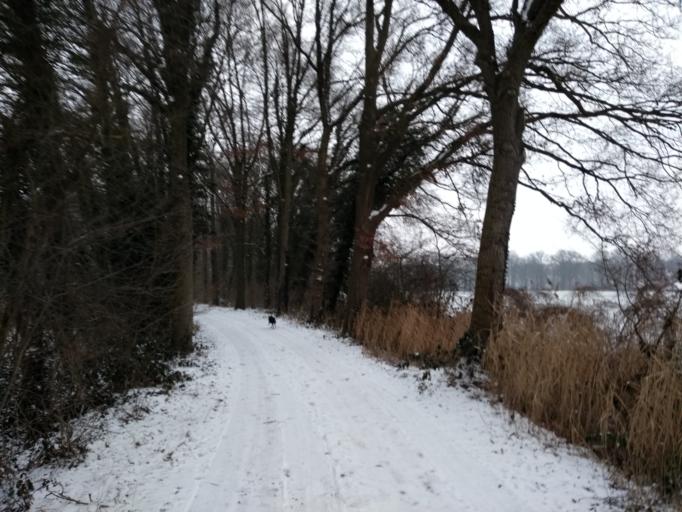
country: NL
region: Overijssel
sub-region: Gemeente Borne
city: Borne
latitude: 52.3238
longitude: 6.7453
